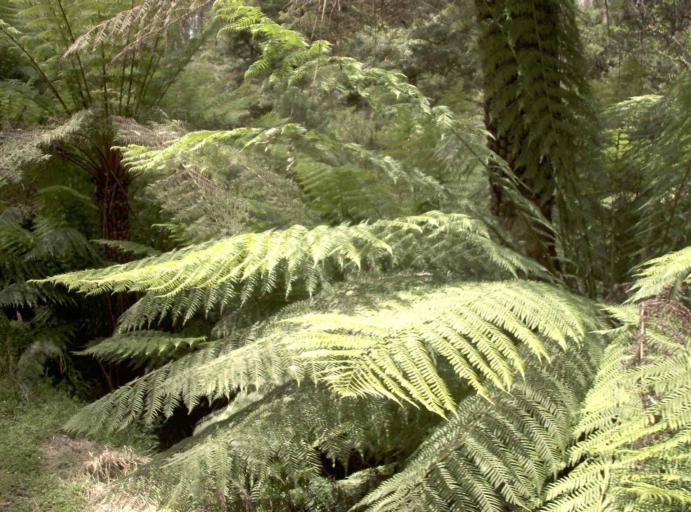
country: AU
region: Victoria
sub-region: Latrobe
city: Traralgon
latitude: -38.4426
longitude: 146.5366
